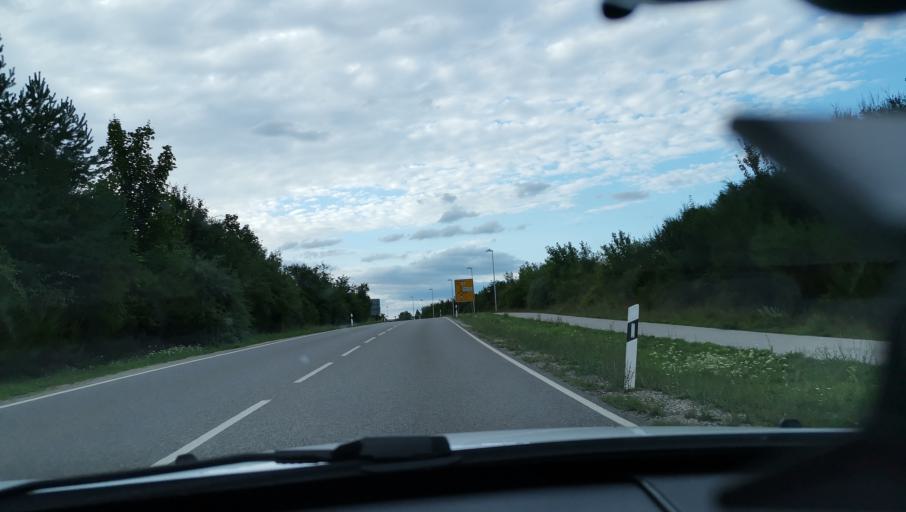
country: DE
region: Bavaria
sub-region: Regierungsbezirk Mittelfranken
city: Zirndorf
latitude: 49.4376
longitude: 10.9383
